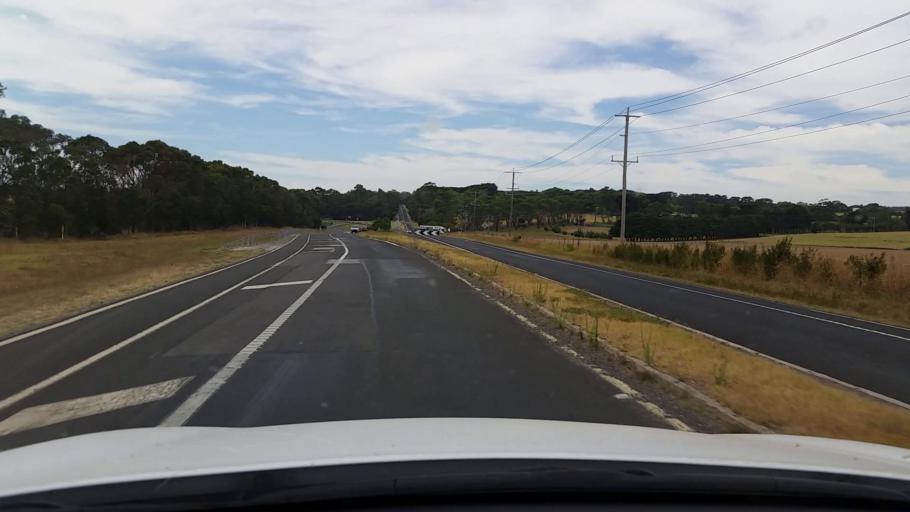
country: AU
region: Victoria
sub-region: Mornington Peninsula
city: Safety Beach
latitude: -38.3122
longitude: 145.0253
